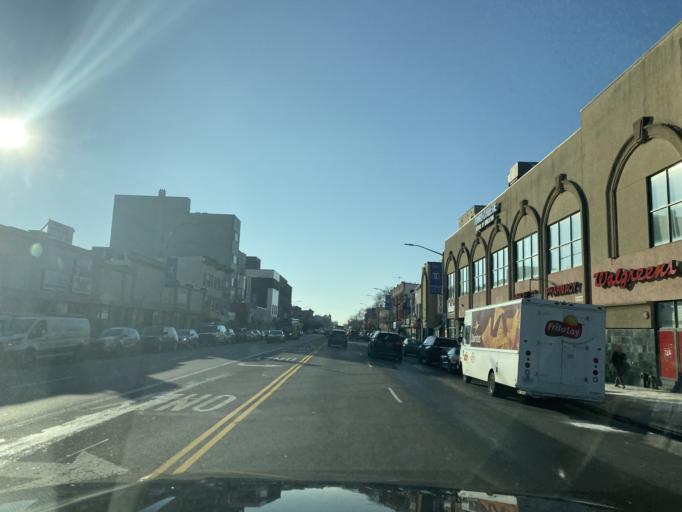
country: US
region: New York
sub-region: Kings County
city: Bensonhurst
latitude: 40.6073
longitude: -73.9619
